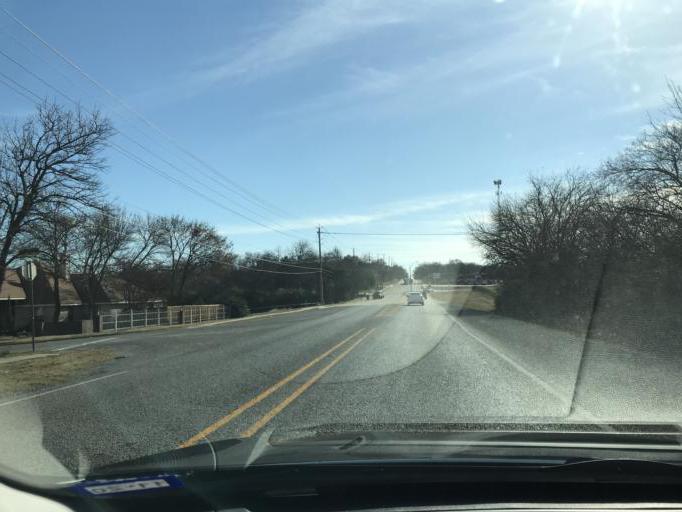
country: US
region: Texas
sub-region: Denton County
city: Denton
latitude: 33.2426
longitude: -97.1318
